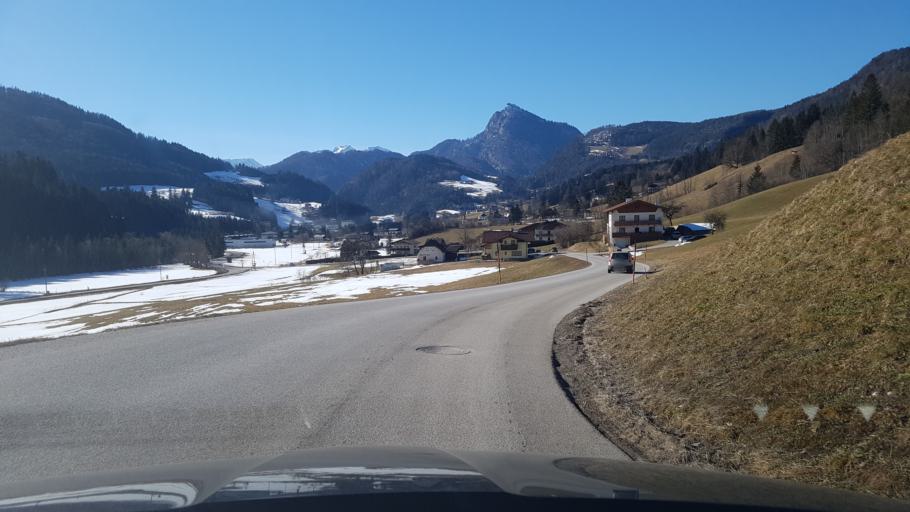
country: AT
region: Salzburg
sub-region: Politischer Bezirk Hallein
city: Abtenau
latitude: 47.5944
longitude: 13.3305
